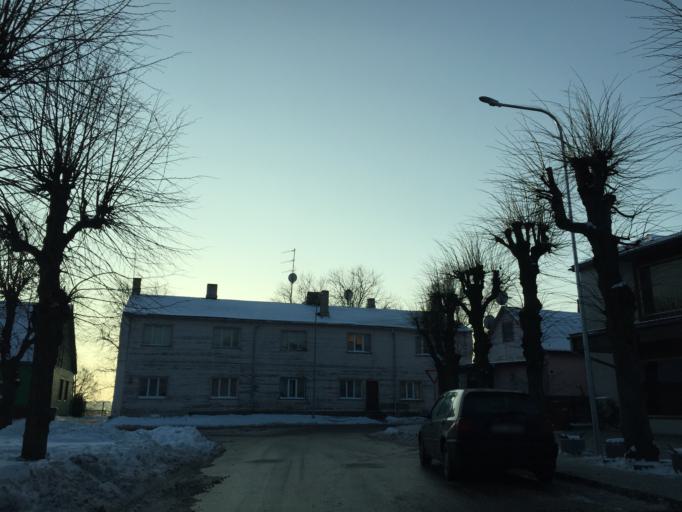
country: LV
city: Tireli
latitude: 56.9424
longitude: 23.6195
